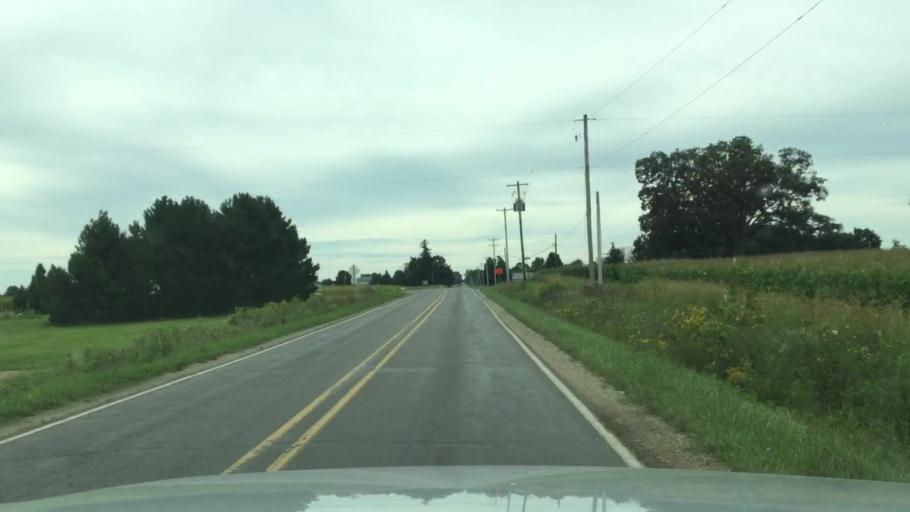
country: US
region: Michigan
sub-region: Shiawassee County
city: Durand
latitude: 42.9517
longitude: -83.9891
